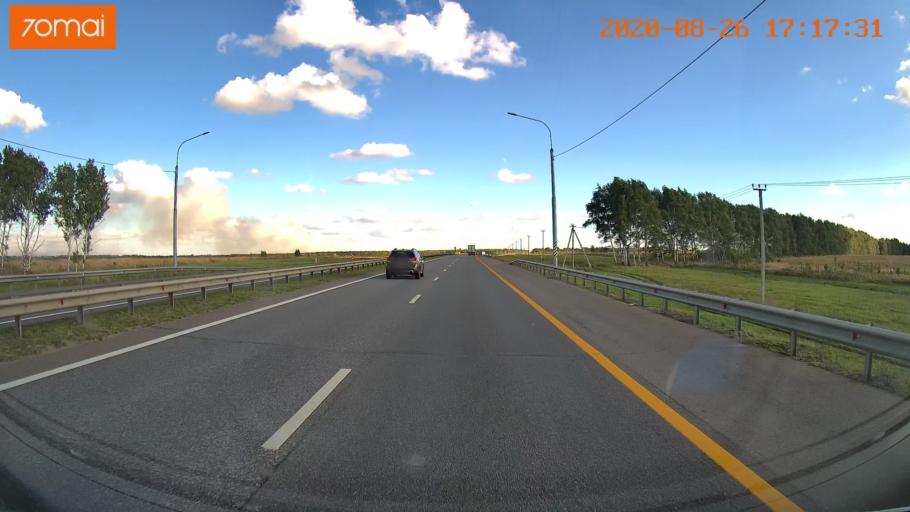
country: RU
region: Tula
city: Volovo
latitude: 53.6230
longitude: 38.0876
